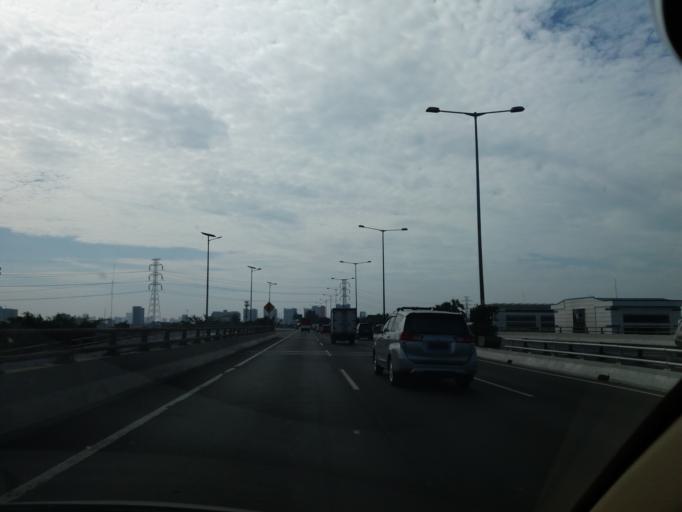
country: ID
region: Jakarta Raya
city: Jakarta
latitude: -6.2083
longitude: 106.8738
